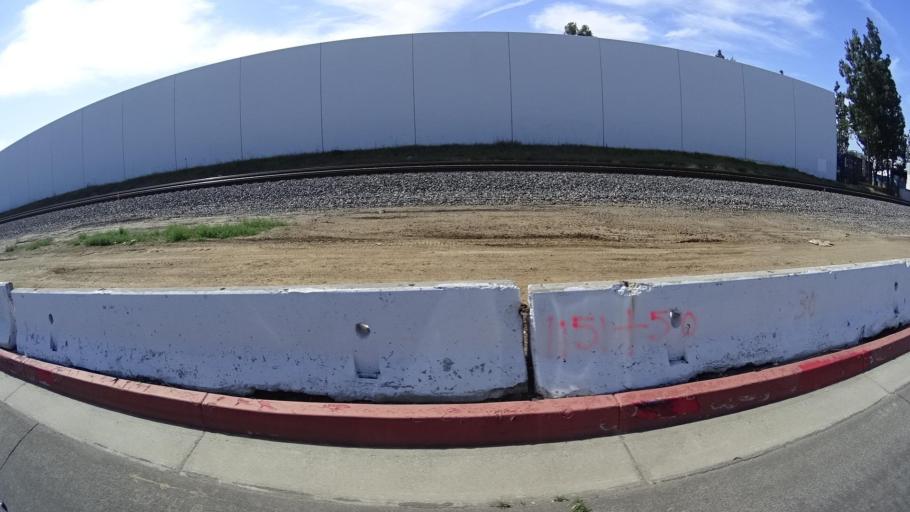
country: US
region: California
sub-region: Los Angeles County
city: South San Jose Hills
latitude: 33.9971
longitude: -117.8986
